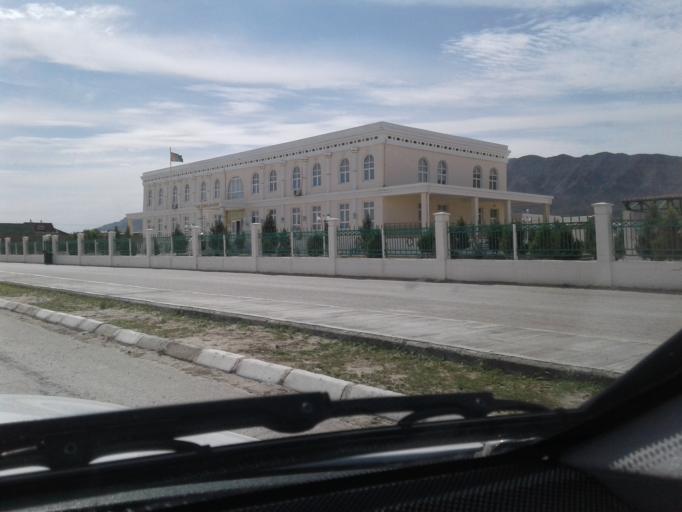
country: TM
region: Balkan
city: Gazanjyk
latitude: 39.2438
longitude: 55.4995
